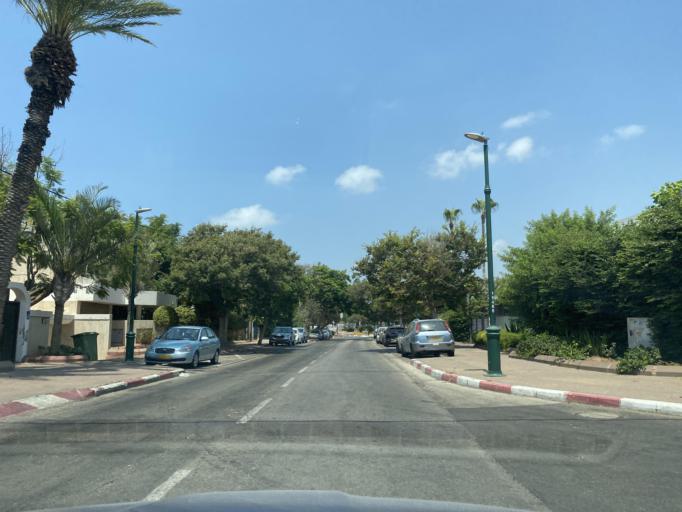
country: IL
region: Tel Aviv
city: Herzliya Pituah
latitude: 32.1742
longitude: 34.8038
